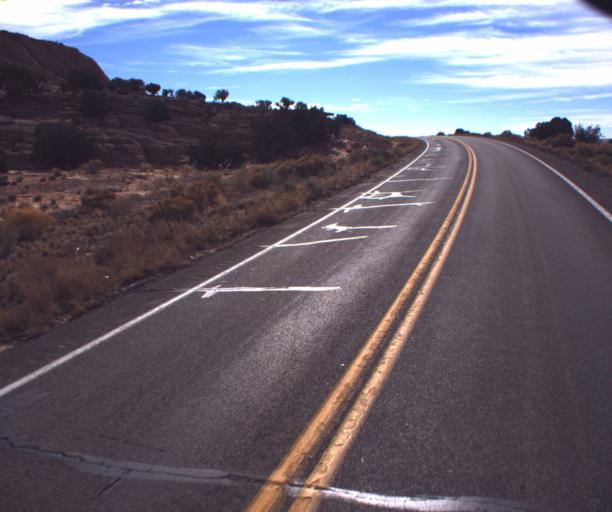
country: US
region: Arizona
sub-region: Coconino County
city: Kaibito
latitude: 36.6712
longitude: -111.2567
